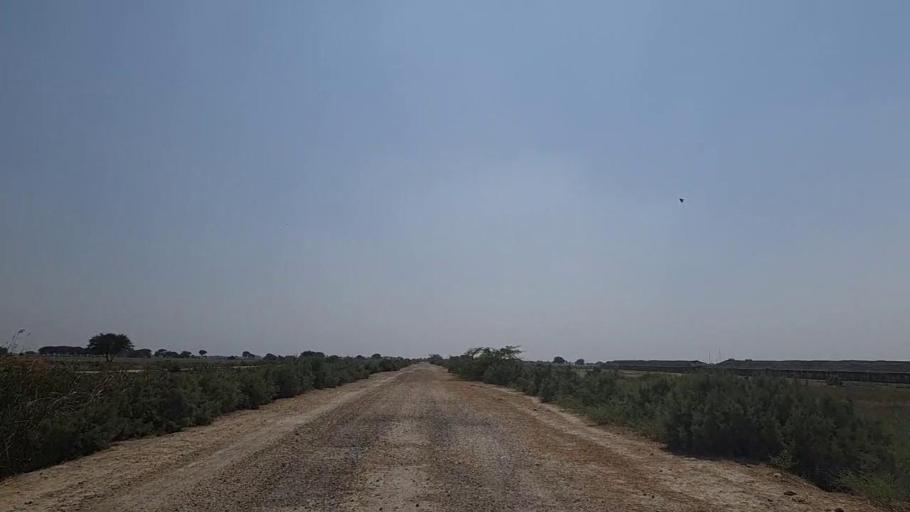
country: PK
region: Sindh
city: Mirpur Batoro
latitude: 24.5464
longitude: 68.3167
